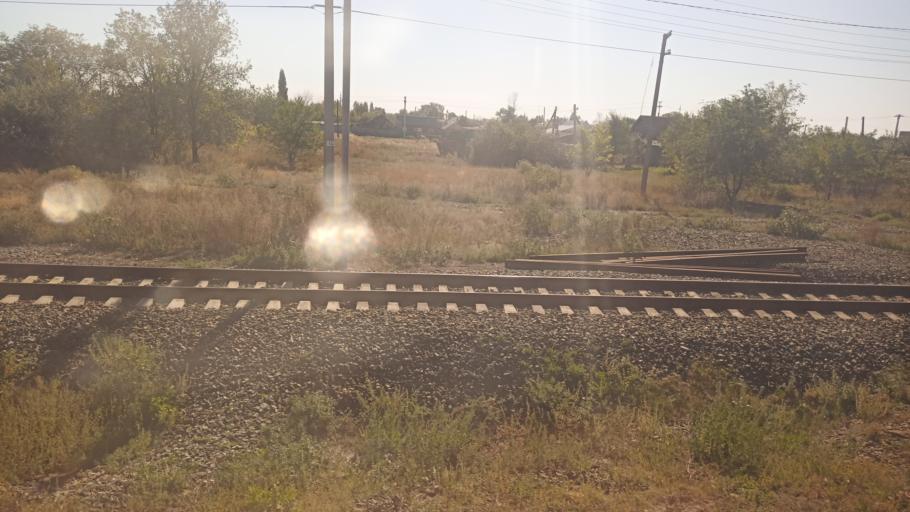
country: RU
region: Saratov
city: Pushkino
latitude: 51.2346
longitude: 46.9830
